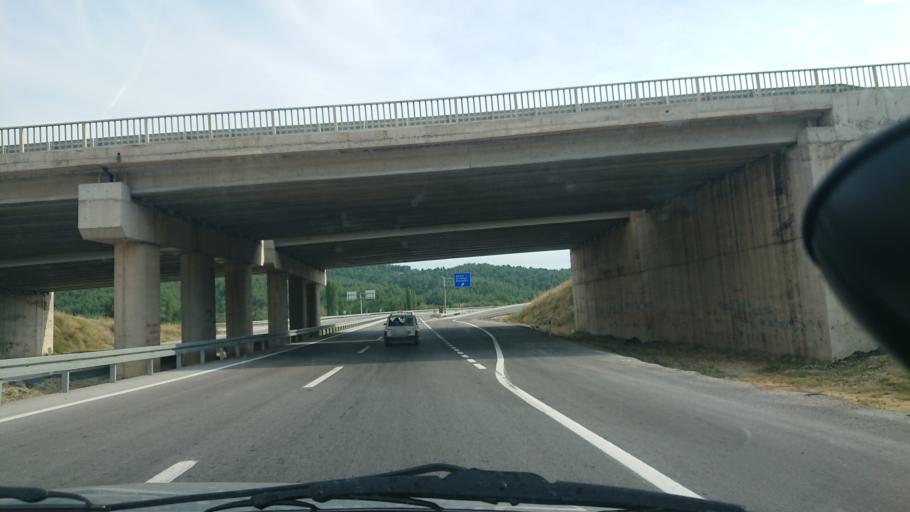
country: TR
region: Kuetahya
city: Gediz
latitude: 38.9354
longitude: 29.3107
